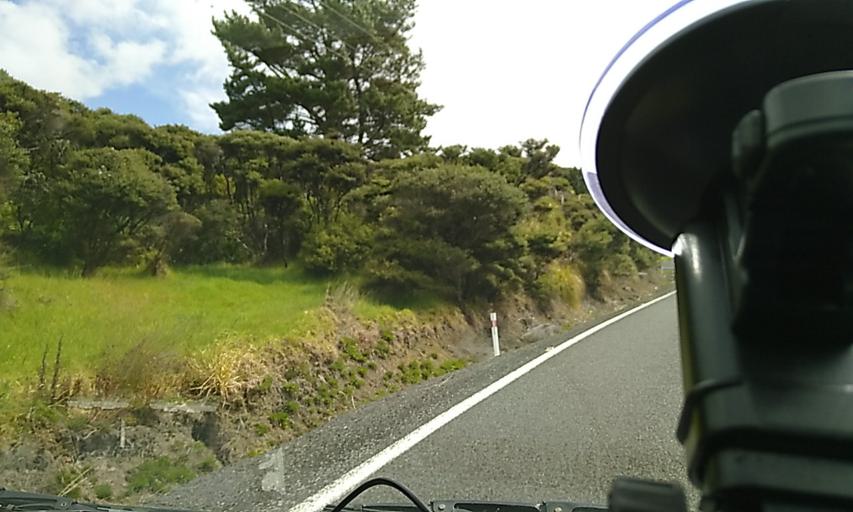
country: NZ
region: Northland
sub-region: Far North District
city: Ahipara
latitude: -35.5394
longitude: 173.3854
